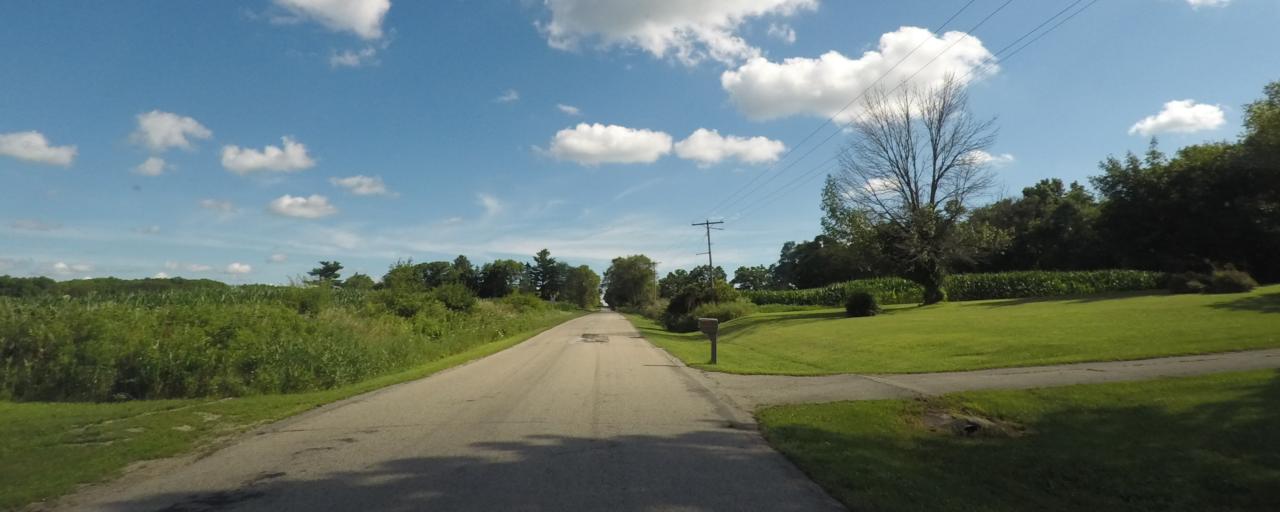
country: US
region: Wisconsin
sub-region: Rock County
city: Edgerton
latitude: 42.8343
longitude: -89.1319
